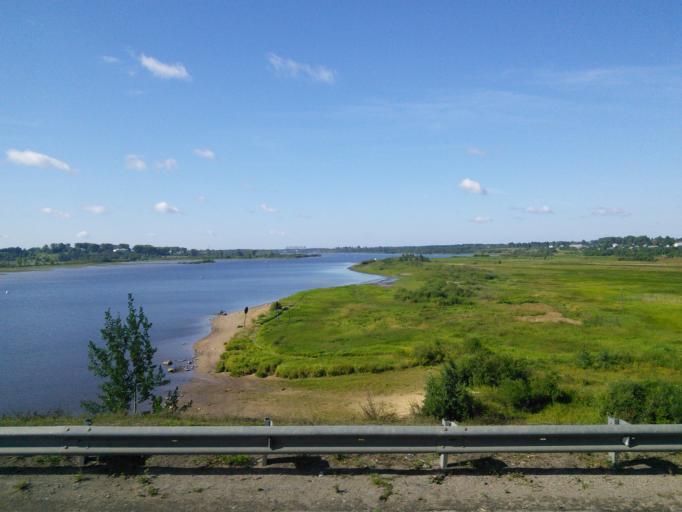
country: RU
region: Vologda
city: Sheksna
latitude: 59.2143
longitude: 38.4930
